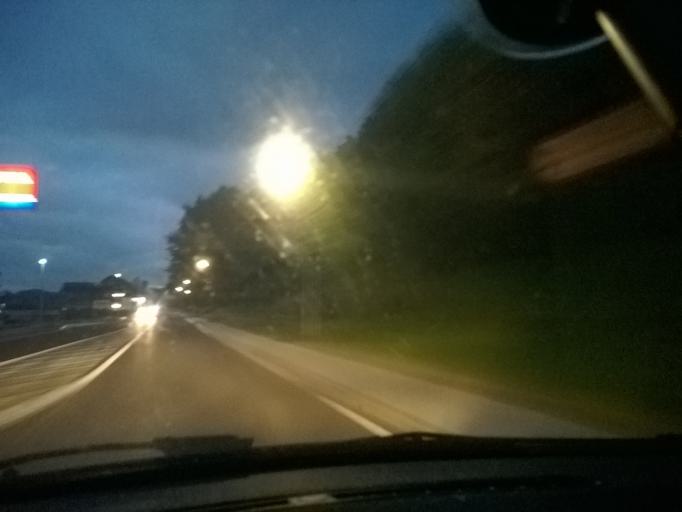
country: SI
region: Rogatec
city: Rogatec
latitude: 46.2264
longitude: 15.6933
